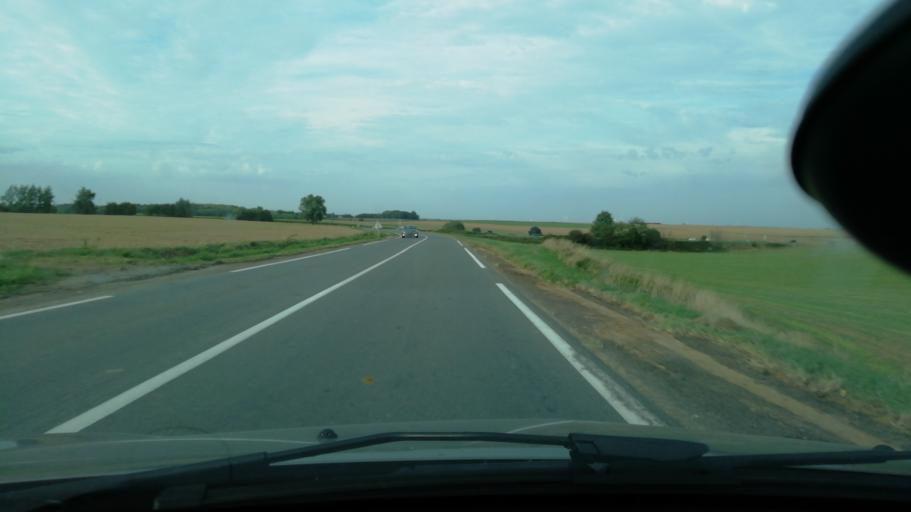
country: FR
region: Nord-Pas-de-Calais
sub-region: Departement du Nord
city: Caudry
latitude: 50.1243
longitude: 3.4408
